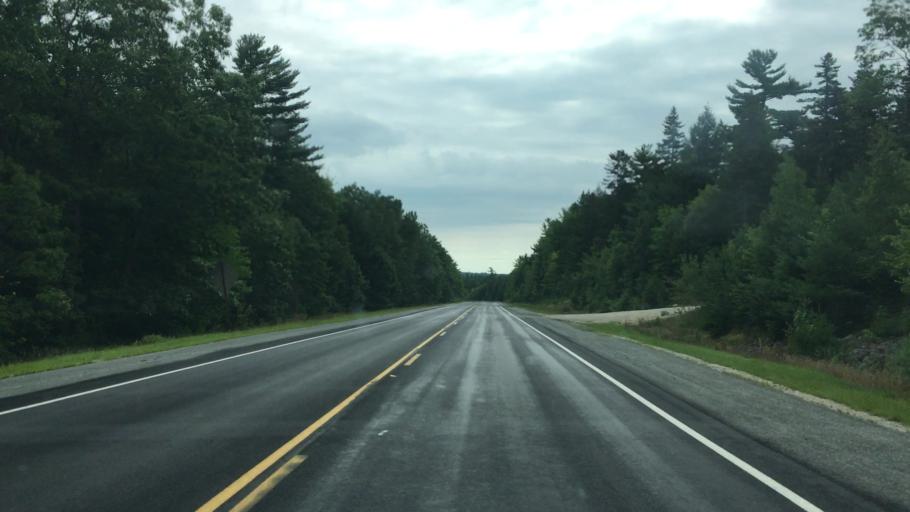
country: US
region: Maine
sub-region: Washington County
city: Addison
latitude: 44.9103
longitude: -67.8498
